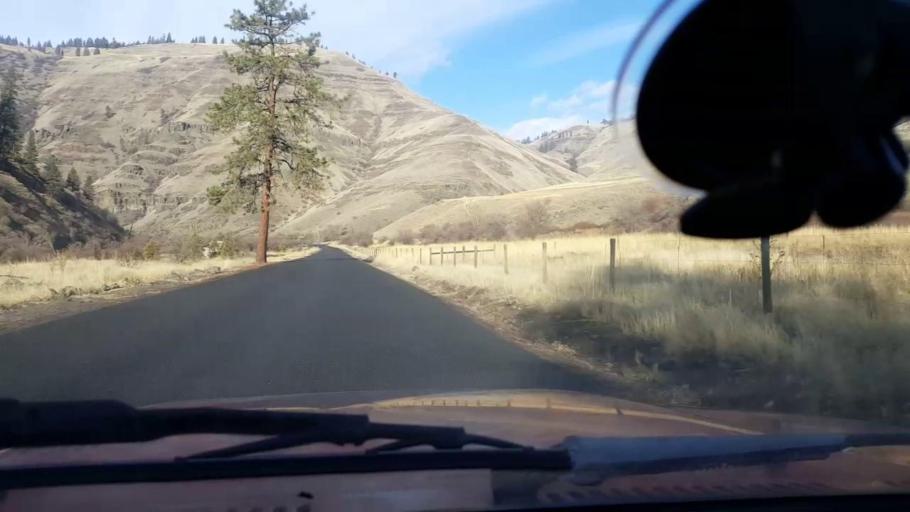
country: US
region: Washington
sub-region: Asotin County
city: Asotin
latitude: 46.0295
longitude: -117.3154
